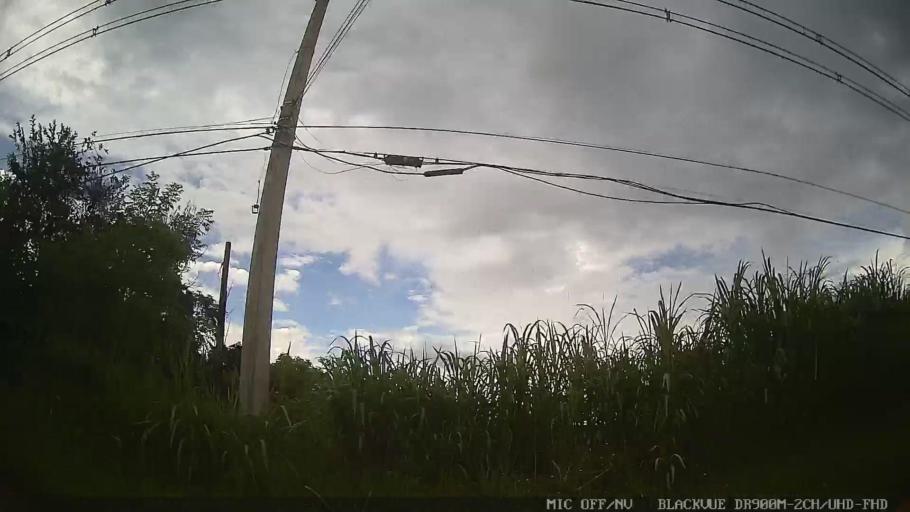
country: BR
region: Sao Paulo
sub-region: Biritiba-Mirim
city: Biritiba Mirim
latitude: -23.5679
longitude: -46.0583
